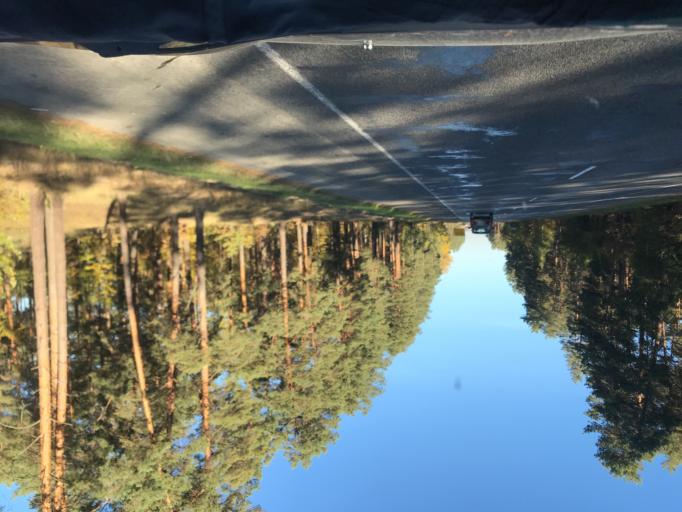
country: BY
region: Gomel
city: Kalinkavichy
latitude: 52.0610
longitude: 29.3611
